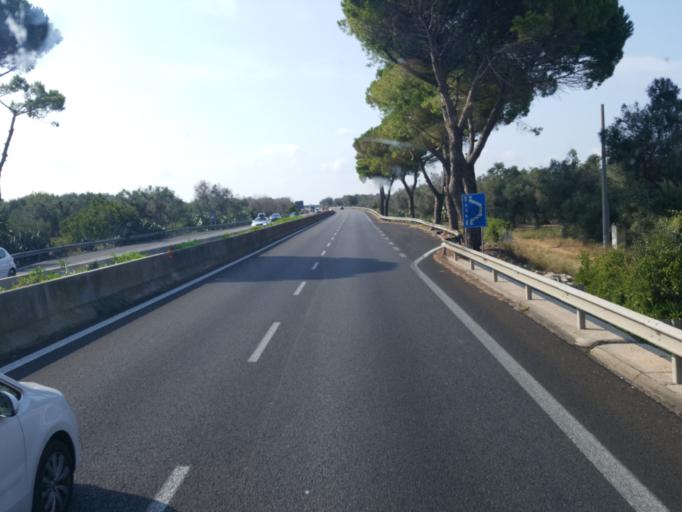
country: IT
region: Apulia
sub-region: Provincia di Lecce
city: Squinzano
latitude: 40.4420
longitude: 18.0766
